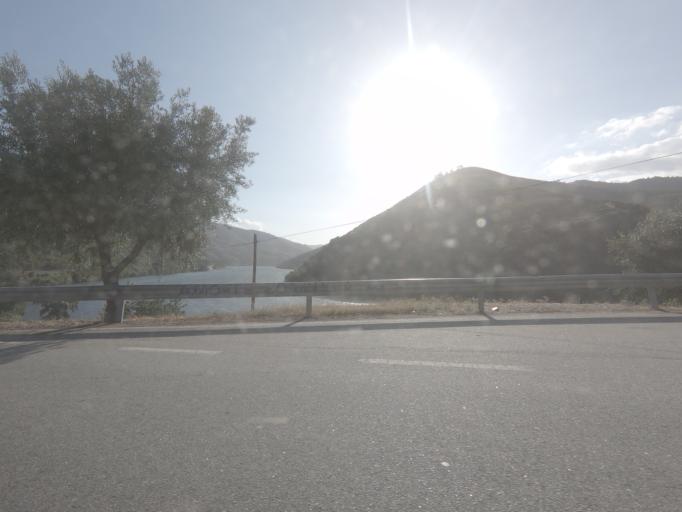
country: PT
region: Viseu
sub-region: Tabuaco
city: Tabuaco
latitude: 41.1617
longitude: -7.5722
